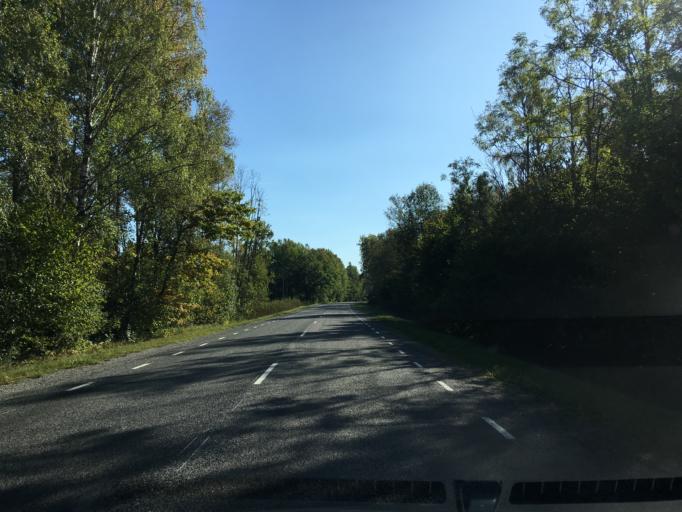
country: EE
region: Laeaene
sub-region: Lihula vald
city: Lihula
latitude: 58.6224
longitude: 23.6909
